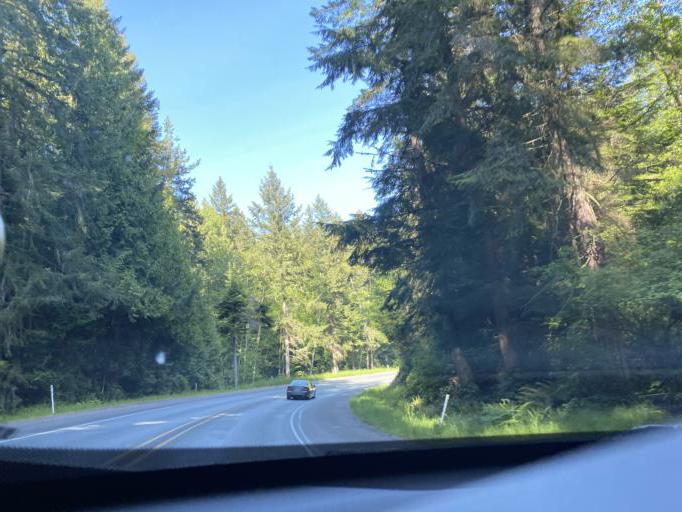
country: US
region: Washington
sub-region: Island County
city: Langley
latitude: 48.0332
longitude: -122.4306
